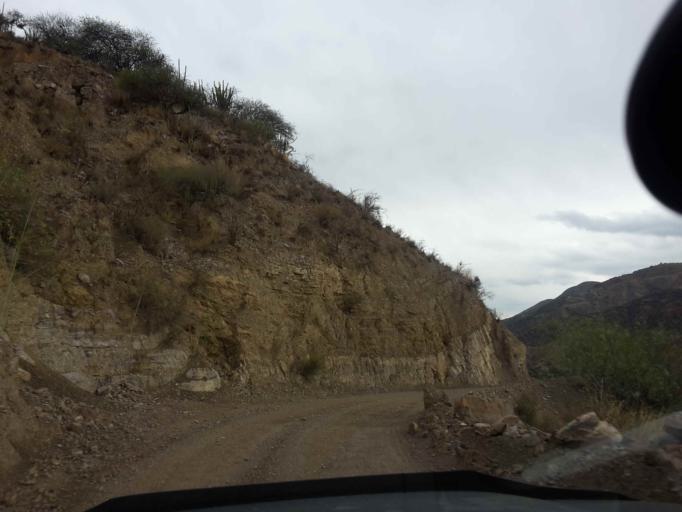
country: BO
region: Cochabamba
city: Sipe Sipe
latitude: -17.5285
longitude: -66.5268
